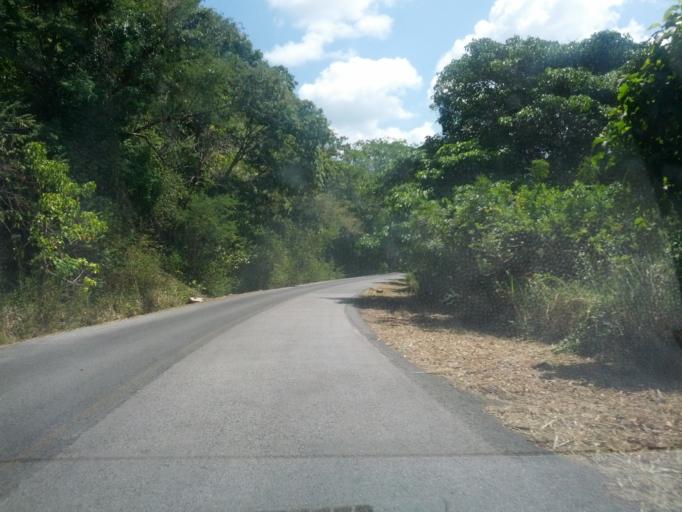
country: CR
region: Puntarenas
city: Ciudad Cortes
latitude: 8.9631
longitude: -83.3150
